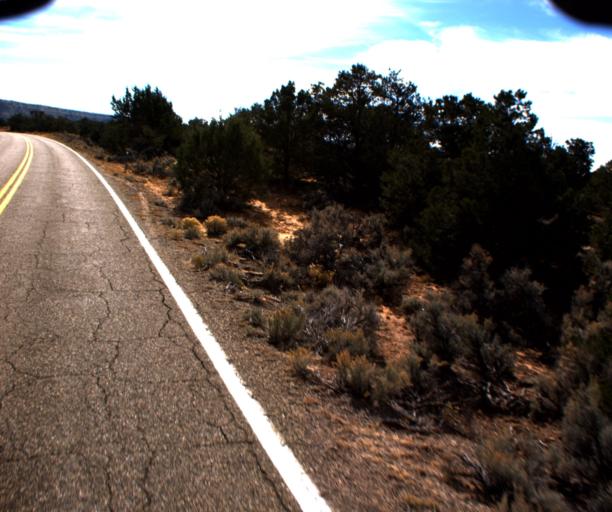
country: US
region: Arizona
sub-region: Navajo County
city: Kayenta
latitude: 36.5898
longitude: -110.4949
